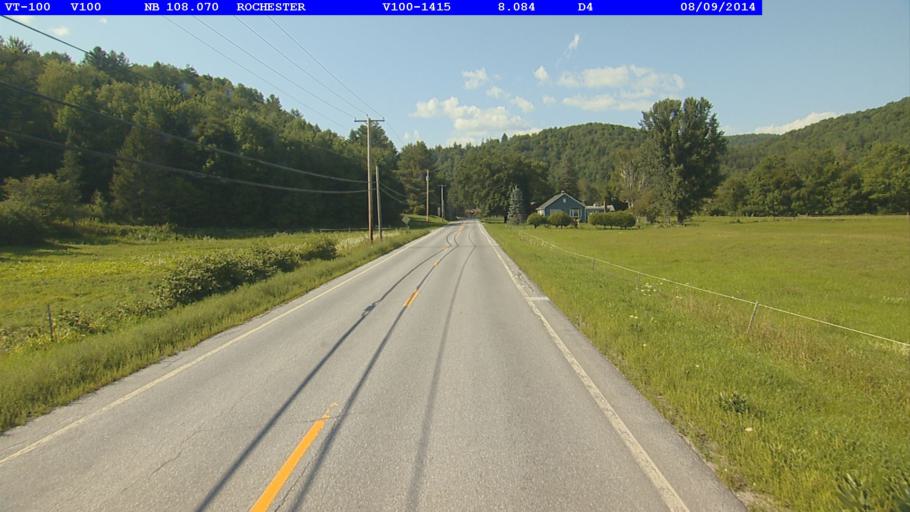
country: US
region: Vermont
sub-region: Orange County
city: Randolph
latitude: 43.9090
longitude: -72.8303
